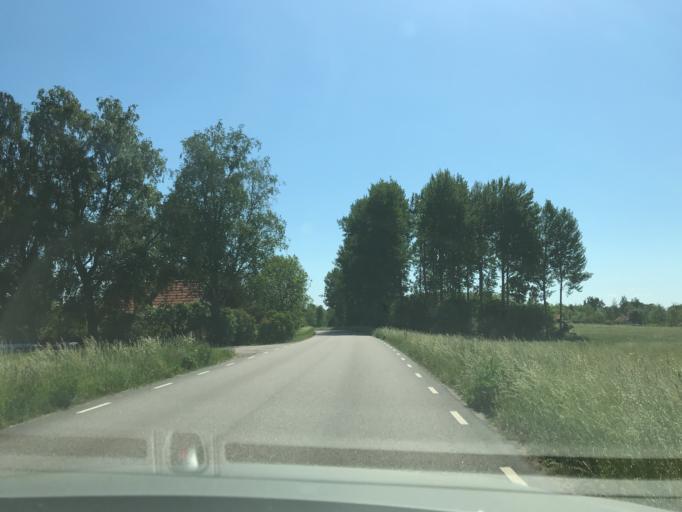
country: SE
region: Vaestra Goetaland
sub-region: Gotene Kommun
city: Kallby
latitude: 58.5356
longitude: 13.3222
